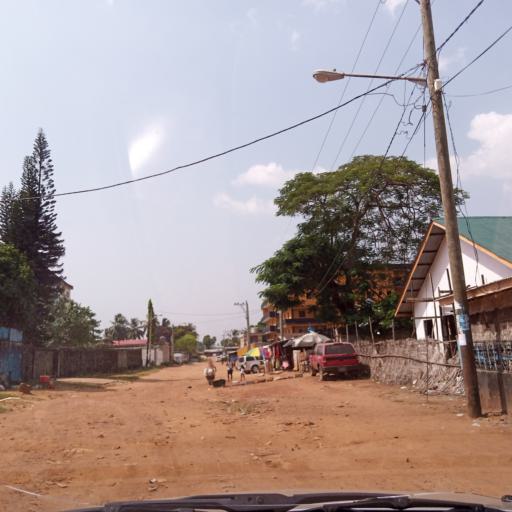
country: LR
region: Montserrado
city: Monrovia
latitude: 6.2894
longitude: -10.7640
